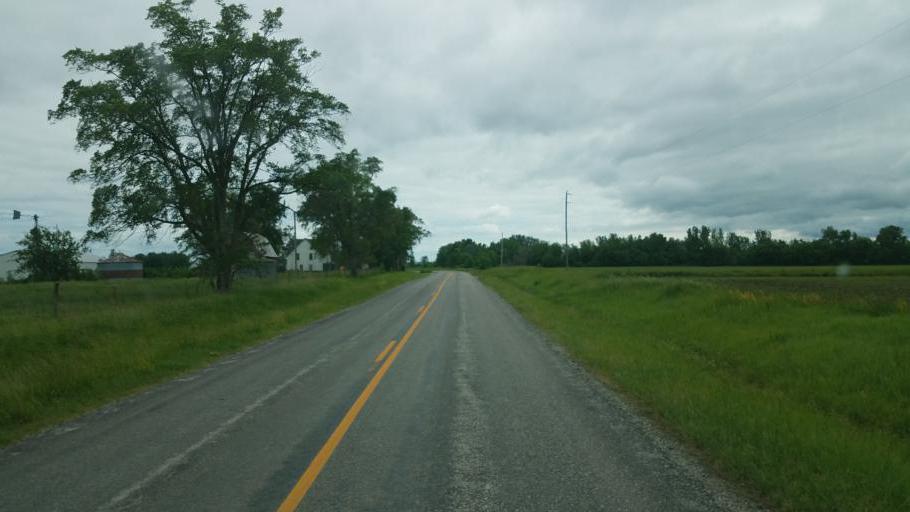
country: US
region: Iowa
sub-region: Decatur County
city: Lamoni
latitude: 40.4999
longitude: -93.8177
